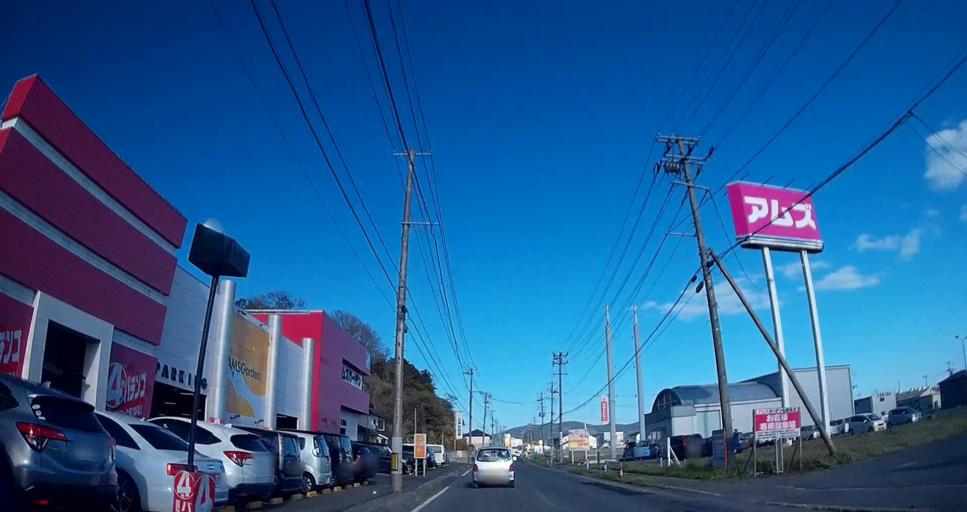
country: JP
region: Miyagi
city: Ishinomaki
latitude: 38.4205
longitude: 141.3275
